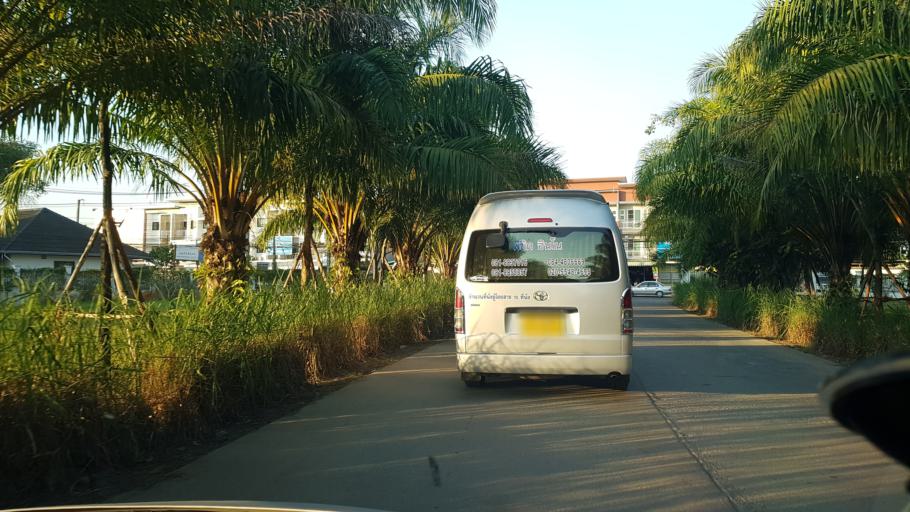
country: TH
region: Chiang Rai
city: Chiang Rai
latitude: 19.9239
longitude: 99.8408
